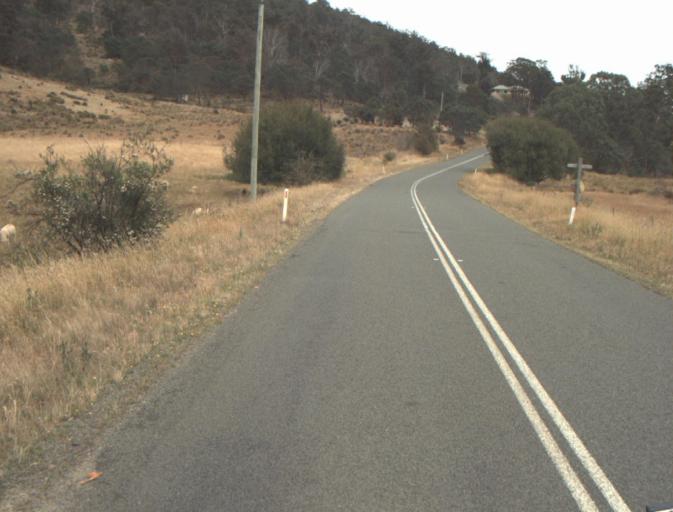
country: AU
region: Tasmania
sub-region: Northern Midlands
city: Evandale
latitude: -41.4987
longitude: 147.4146
